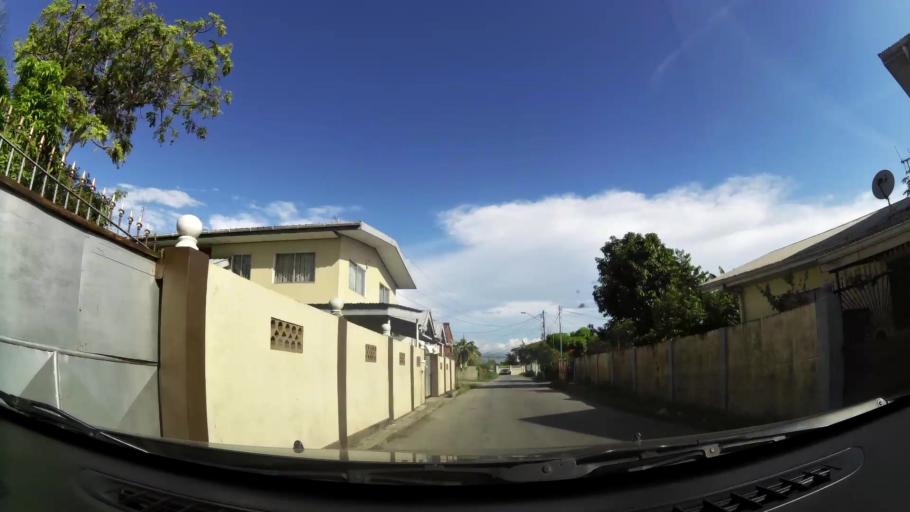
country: TT
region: Chaguanas
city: Chaguanas
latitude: 10.5253
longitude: -61.3904
